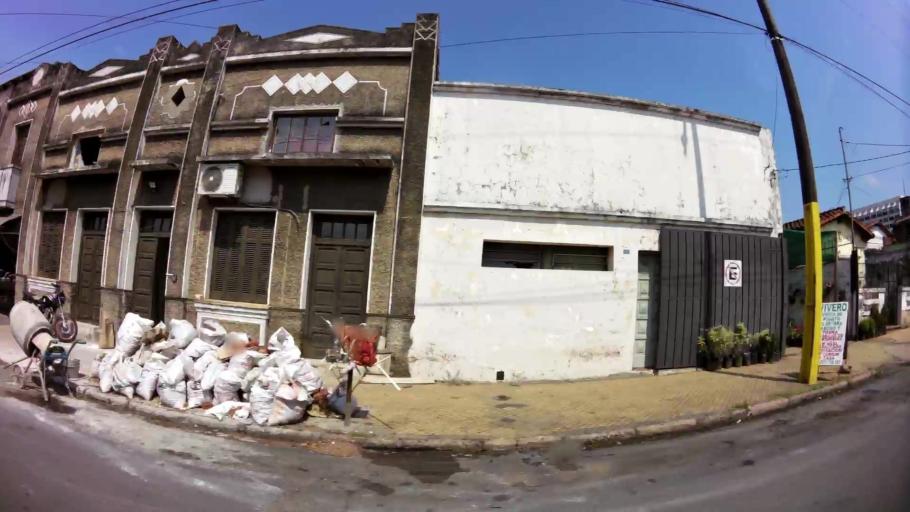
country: PY
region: Asuncion
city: Asuncion
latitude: -25.2891
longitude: -57.6530
